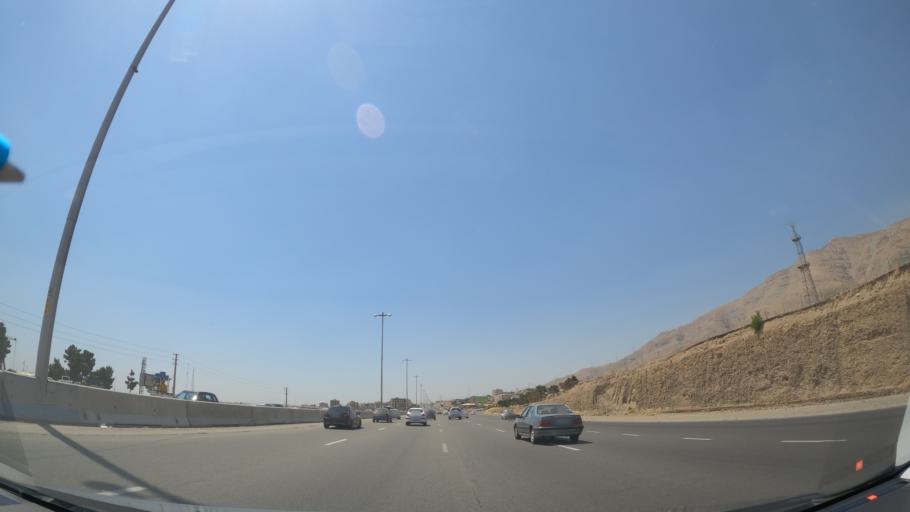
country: IR
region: Tehran
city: Shahr-e Qods
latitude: 35.7508
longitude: 51.0802
